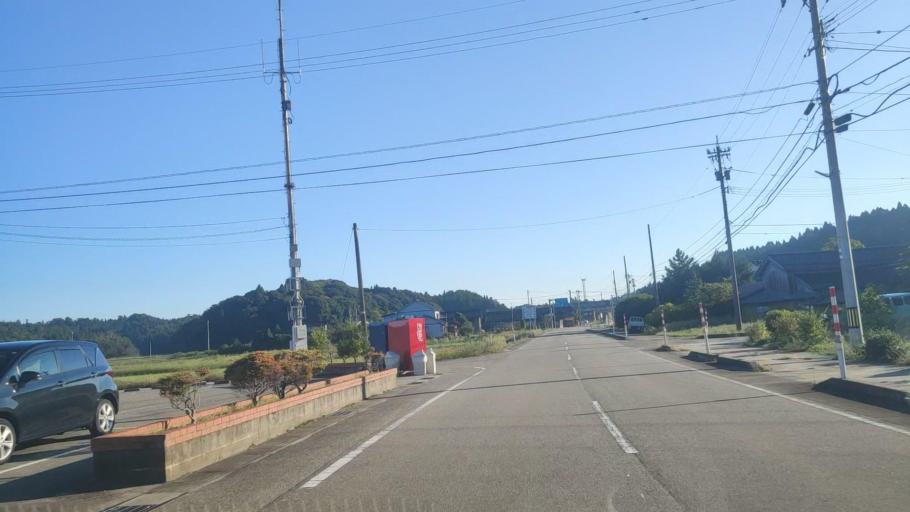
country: JP
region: Ishikawa
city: Nanao
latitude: 37.1350
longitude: 137.0002
